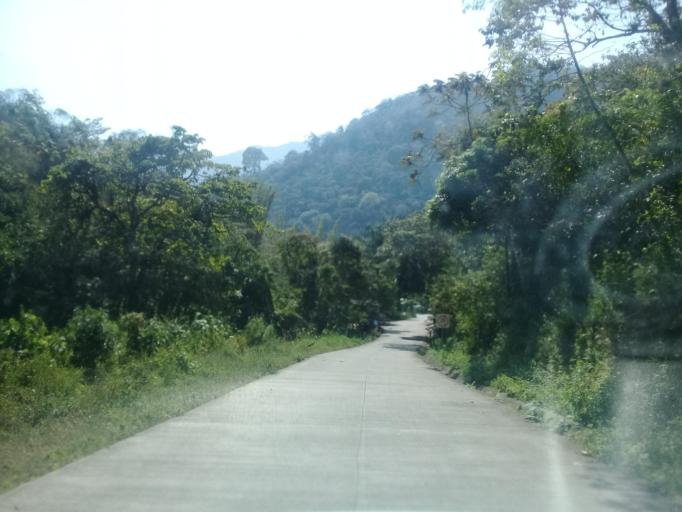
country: MX
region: Veracruz
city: Rafael Delgado
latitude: 18.7810
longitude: -97.0234
